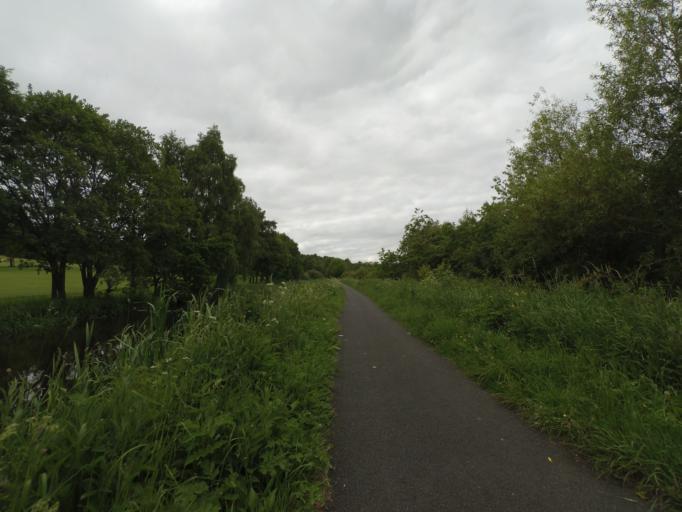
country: GB
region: Scotland
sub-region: West Lothian
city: Linlithgow
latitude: 55.9675
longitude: -3.6203
